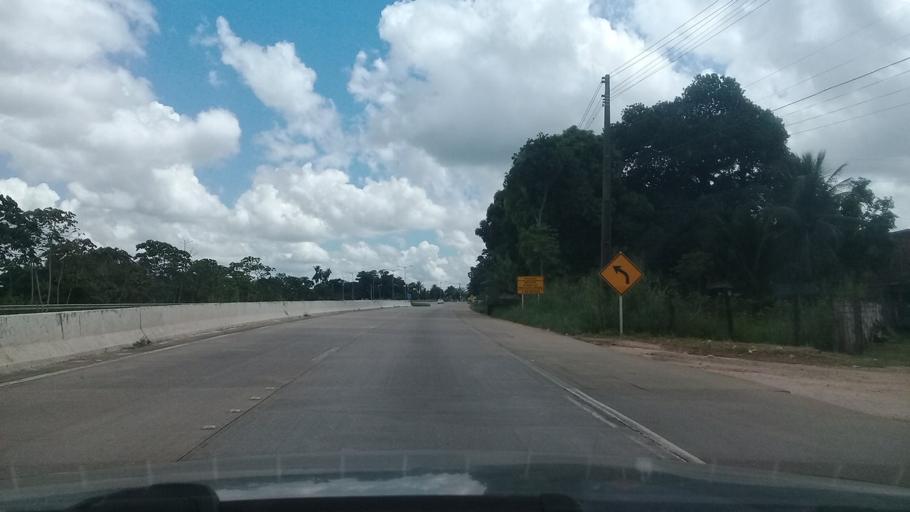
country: BR
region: Pernambuco
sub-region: Sao Lourenco Da Mata
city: Sao Lourenco da Mata
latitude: -7.9363
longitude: -35.1285
